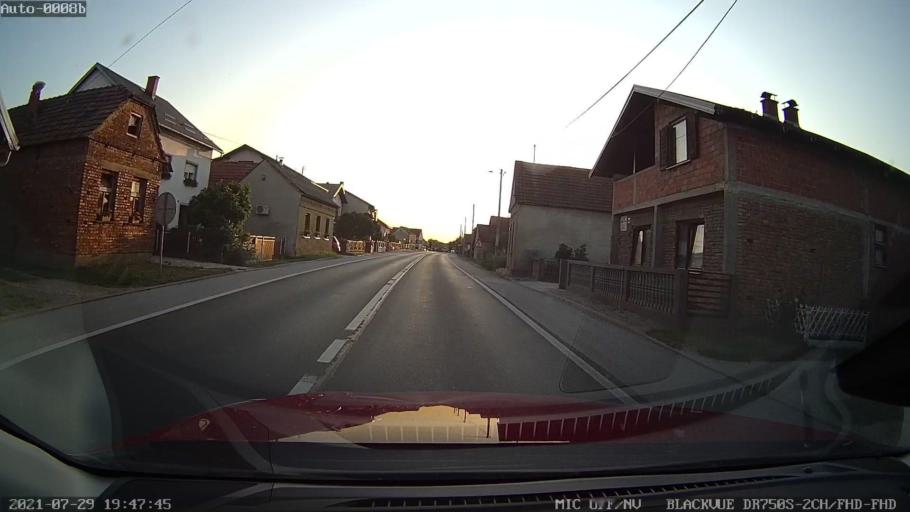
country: HR
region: Varazdinska
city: Ludbreg
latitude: 46.2644
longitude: 16.5563
